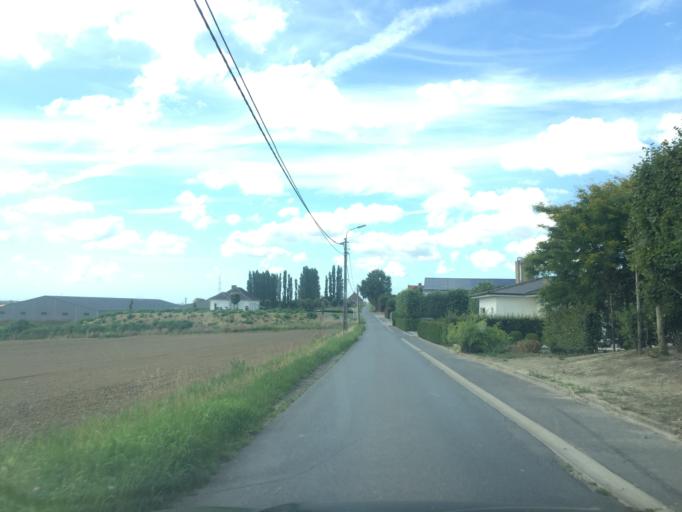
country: BE
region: Flanders
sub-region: Provincie West-Vlaanderen
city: Staden
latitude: 50.9514
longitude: 3.0075
